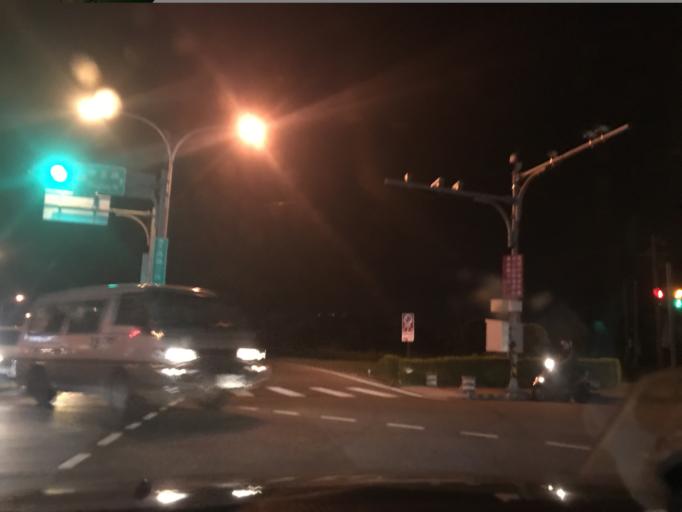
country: TW
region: Taiwan
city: Daxi
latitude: 24.8564
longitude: 121.2195
